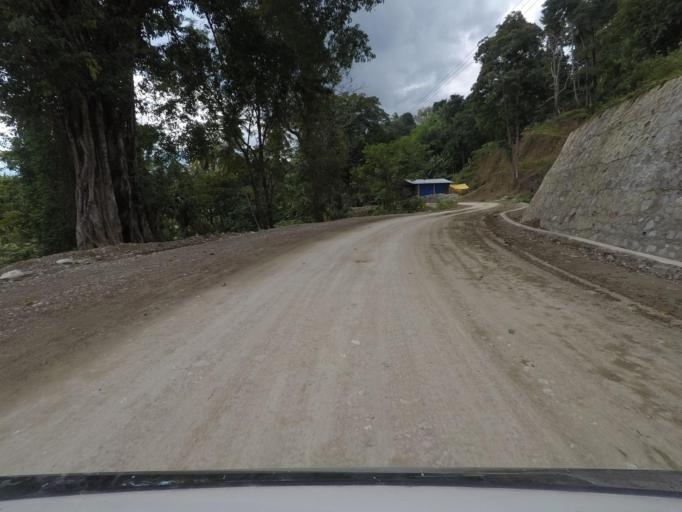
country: TL
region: Viqueque
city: Viqueque
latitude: -8.7859
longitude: 126.3763
